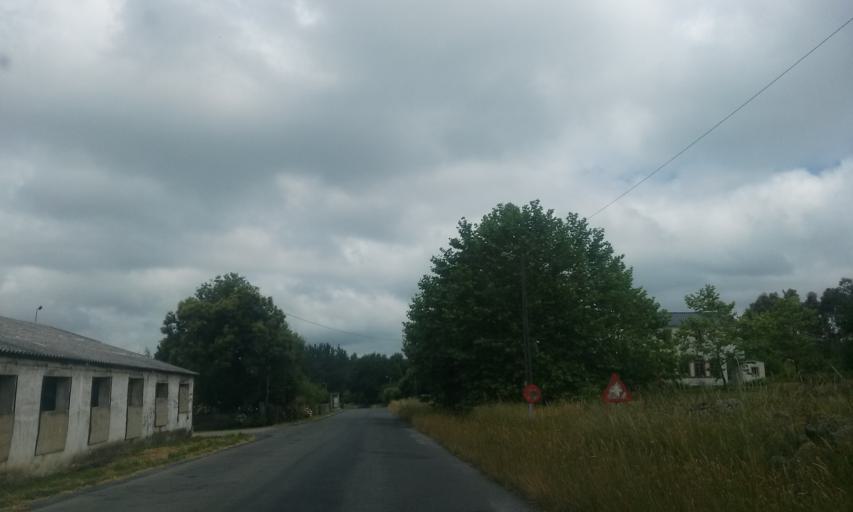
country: ES
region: Galicia
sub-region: Provincia de Lugo
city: Friol
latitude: 43.0859
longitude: -7.8114
